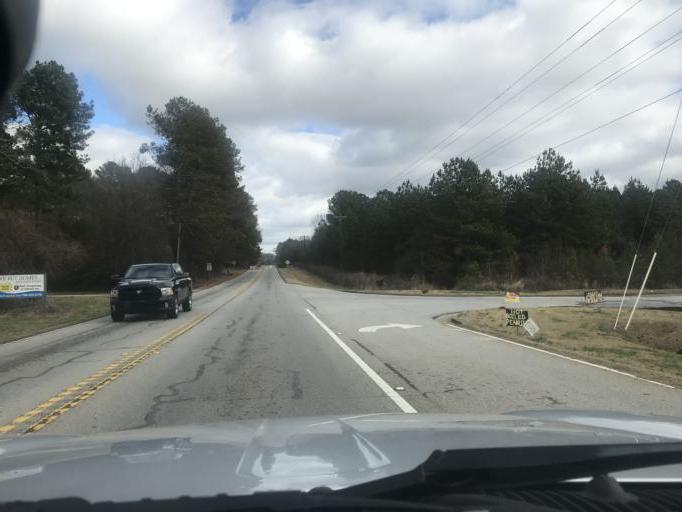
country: US
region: Georgia
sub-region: Barrow County
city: Russell
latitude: 34.0255
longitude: -83.6759
